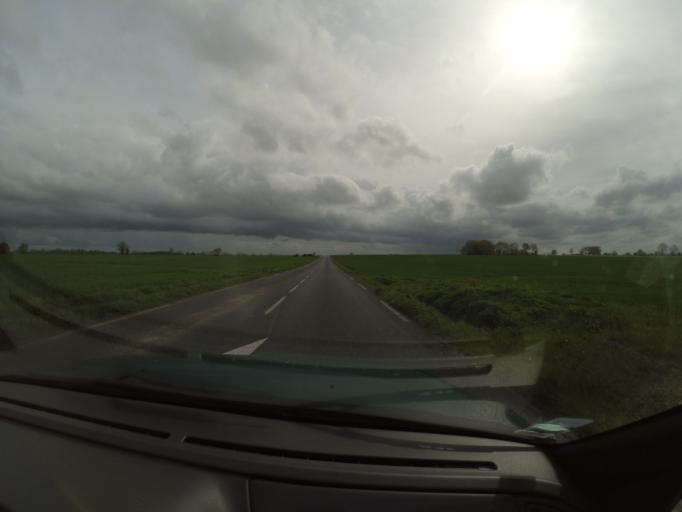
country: FR
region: Pays de la Loire
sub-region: Departement de Maine-et-Loire
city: Saint-Laurent-des-Autels
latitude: 47.2547
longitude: -1.2053
